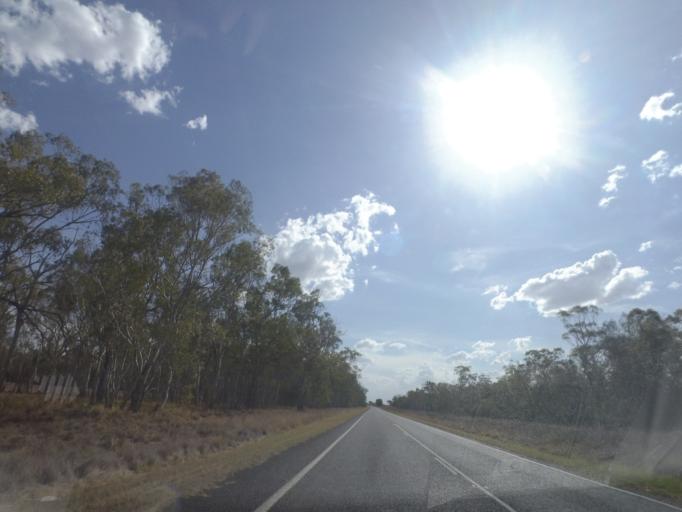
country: AU
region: New South Wales
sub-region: Moree Plains
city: Boggabilla
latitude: -28.5465
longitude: 150.8758
